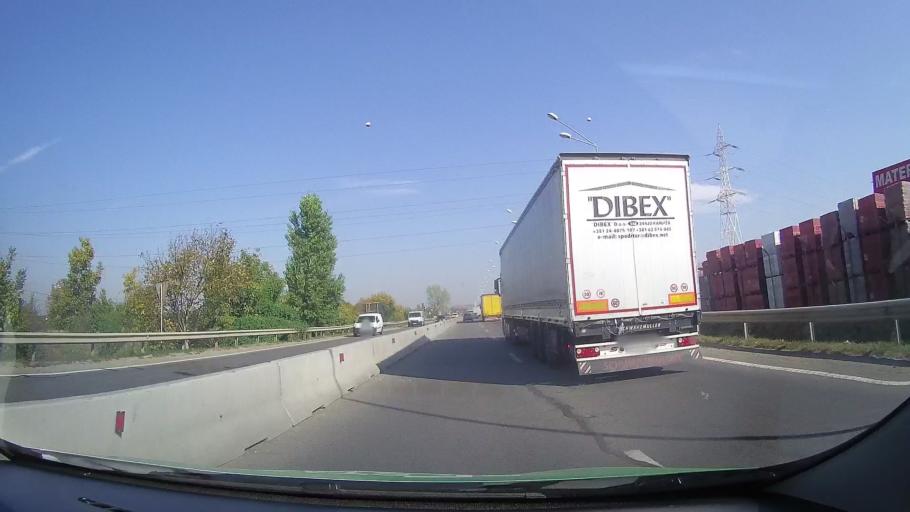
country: RO
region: Bihor
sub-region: Comuna Santandrei
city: Santandrei
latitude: 47.0514
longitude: 21.8867
